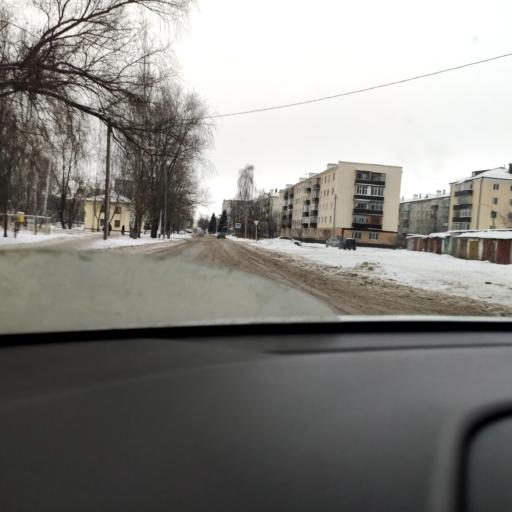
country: RU
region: Tatarstan
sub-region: Zelenodol'skiy Rayon
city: Zelenodolsk
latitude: 55.8537
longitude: 48.4826
